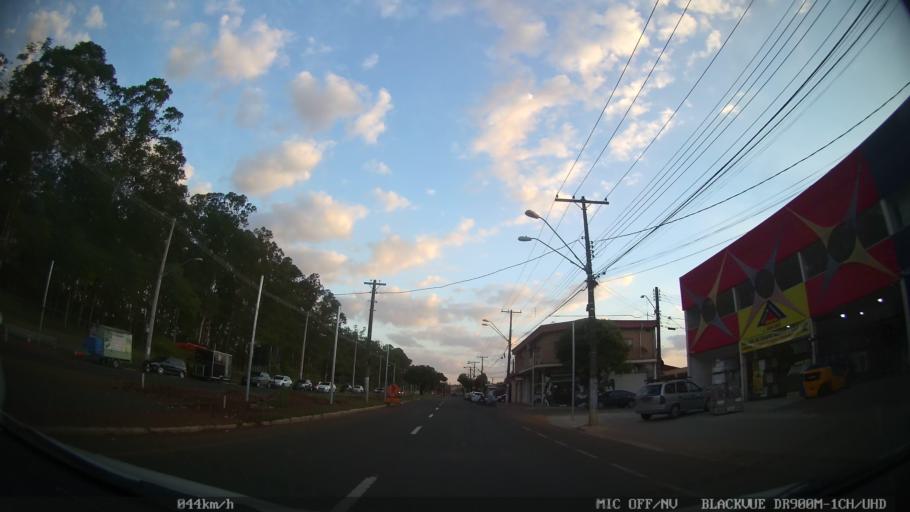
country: BR
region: Sao Paulo
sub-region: Ribeirao Preto
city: Ribeirao Preto
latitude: -21.1566
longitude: -47.7844
